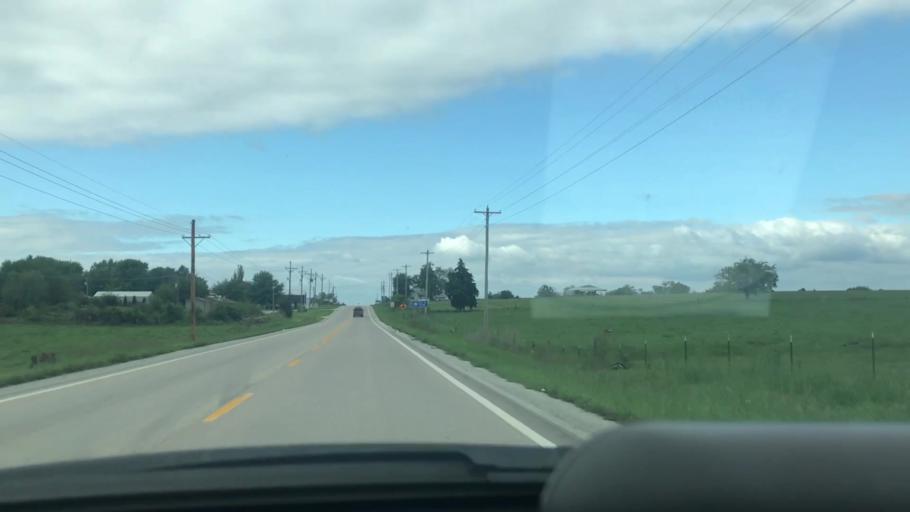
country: US
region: Missouri
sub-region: Hickory County
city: Hermitage
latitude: 37.9357
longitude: -93.2083
